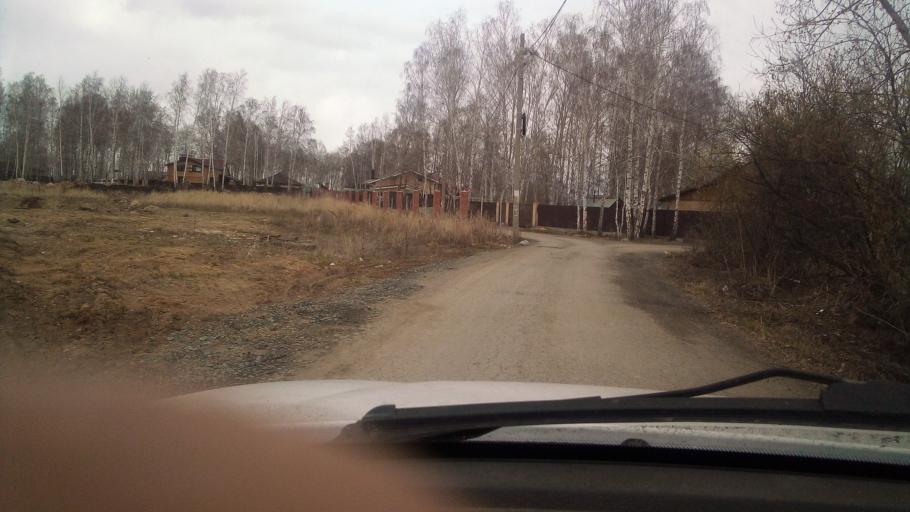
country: RU
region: Chelyabinsk
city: Sargazy
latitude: 55.1285
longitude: 61.2410
